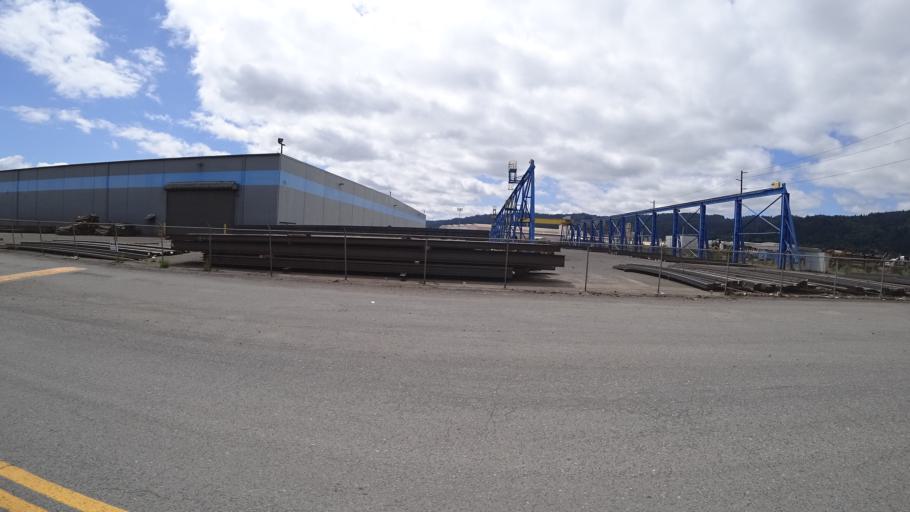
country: US
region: Oregon
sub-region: Washington County
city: West Haven
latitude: 45.6126
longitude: -122.7721
